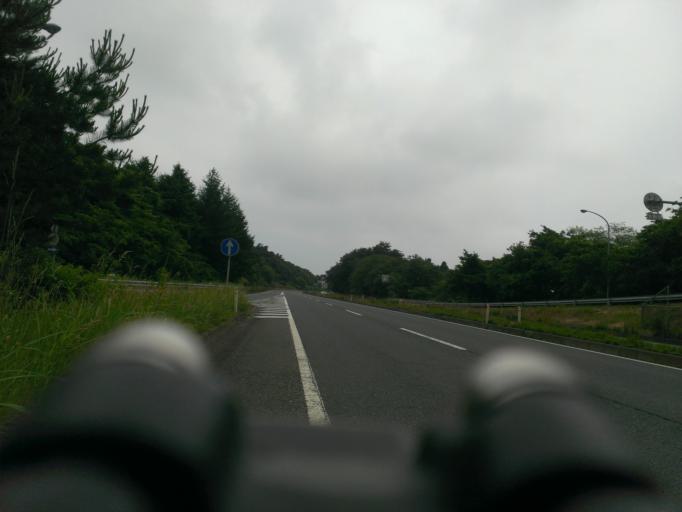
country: JP
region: Iwate
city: Morioka-shi
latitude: 39.7971
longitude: 141.1234
